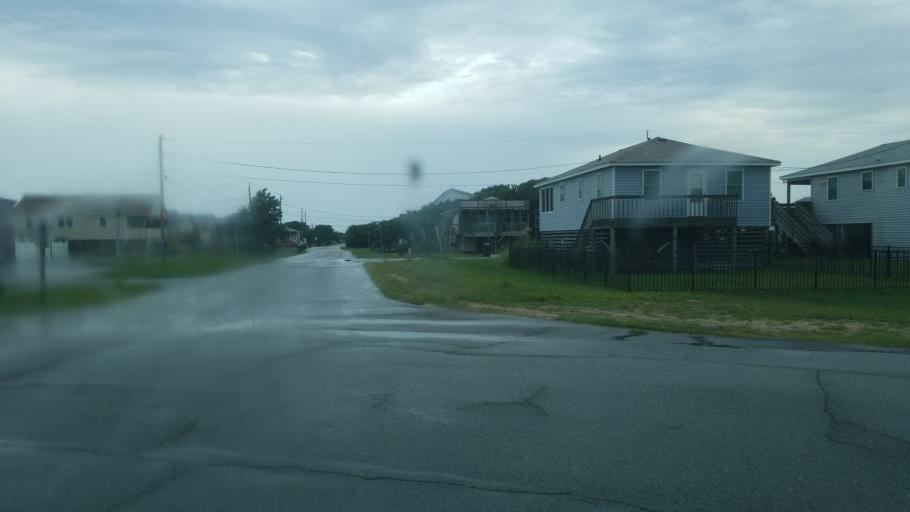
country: US
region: North Carolina
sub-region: Dare County
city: Nags Head
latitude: 35.9828
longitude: -75.6414
